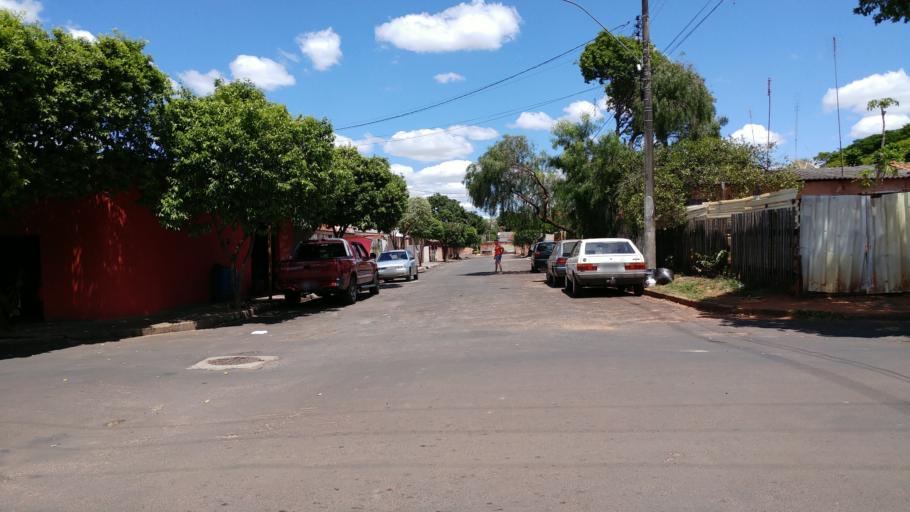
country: BR
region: Sao Paulo
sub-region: Paraguacu Paulista
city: Paraguacu Paulista
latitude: -22.4091
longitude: -50.5699
